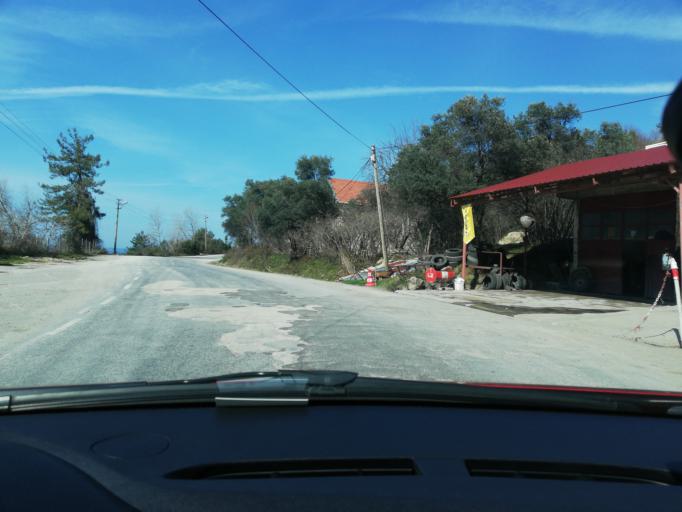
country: TR
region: Bartin
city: Kurucasile
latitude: 41.8383
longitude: 32.7116
